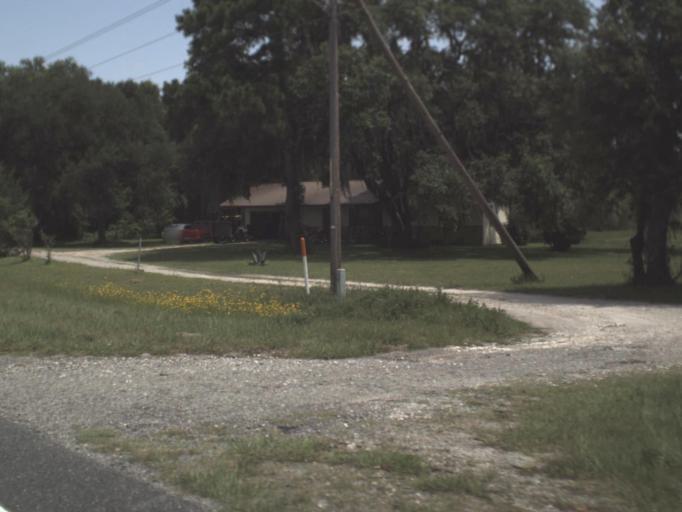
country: US
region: Florida
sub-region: Taylor County
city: Perry
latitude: 30.0241
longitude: -83.5365
